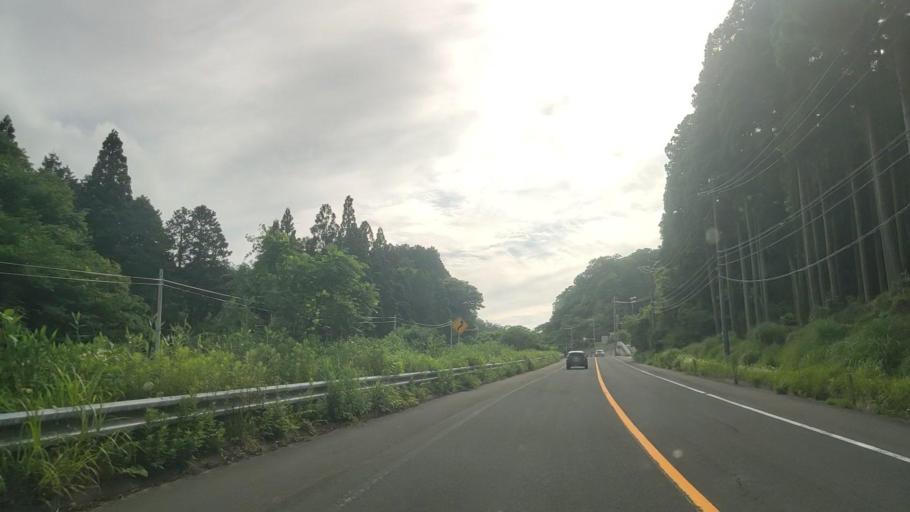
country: JP
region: Kyoto
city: Miyazu
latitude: 35.6589
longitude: 135.0056
